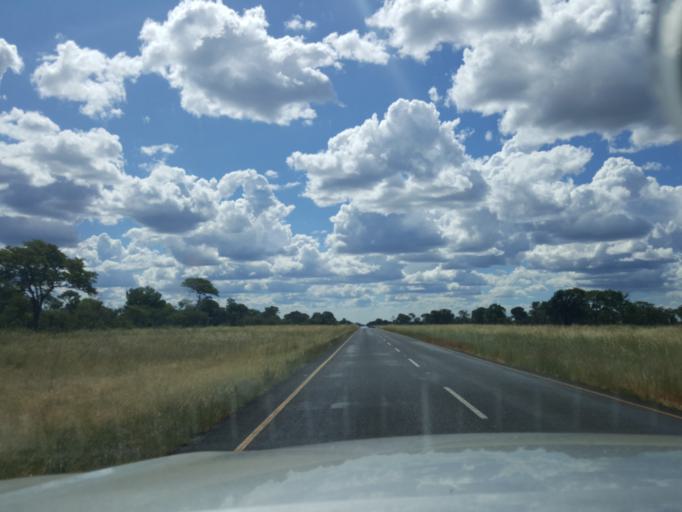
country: BW
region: North West
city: Kasane
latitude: -18.1114
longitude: 25.3245
